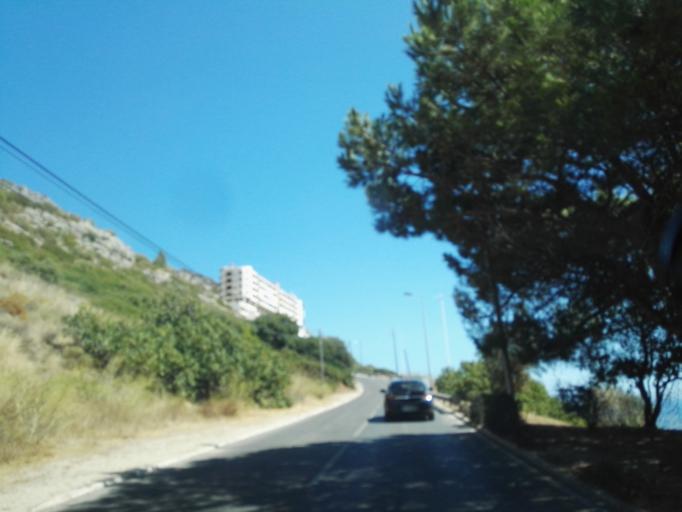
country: PT
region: Setubal
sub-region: Sesimbra
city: Sesimbra
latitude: 38.4438
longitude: -9.0934
